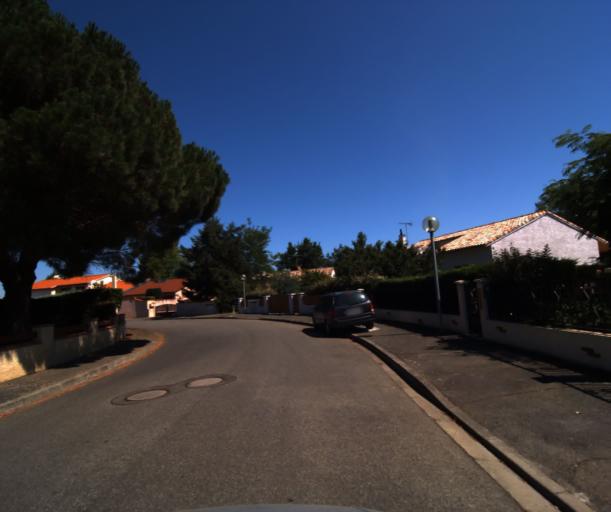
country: FR
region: Midi-Pyrenees
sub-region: Departement de la Haute-Garonne
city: Muret
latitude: 43.4712
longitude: 1.3234
